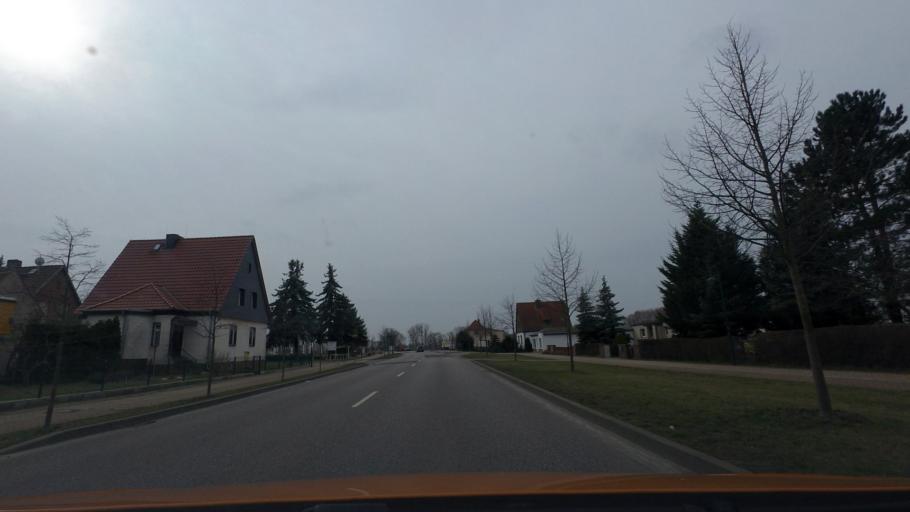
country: DE
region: Saxony-Anhalt
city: Gerwisch
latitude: 52.1713
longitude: 11.7442
